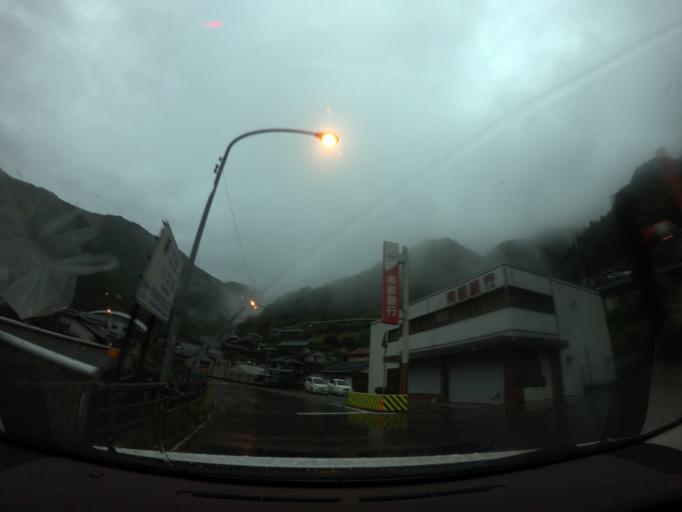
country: JP
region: Wakayama
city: Shingu
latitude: 33.9485
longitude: 135.8041
